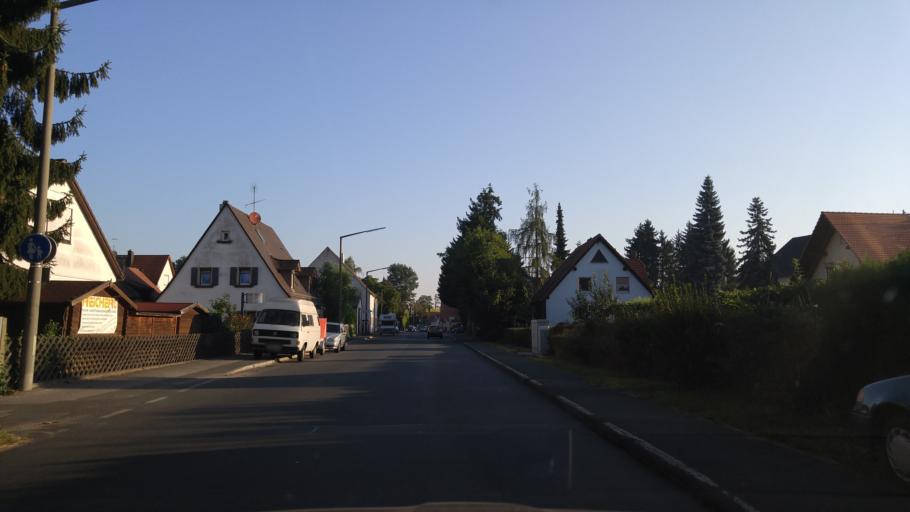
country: DE
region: Bavaria
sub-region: Regierungsbezirk Mittelfranken
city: Erlangen
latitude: 49.5496
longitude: 10.9873
